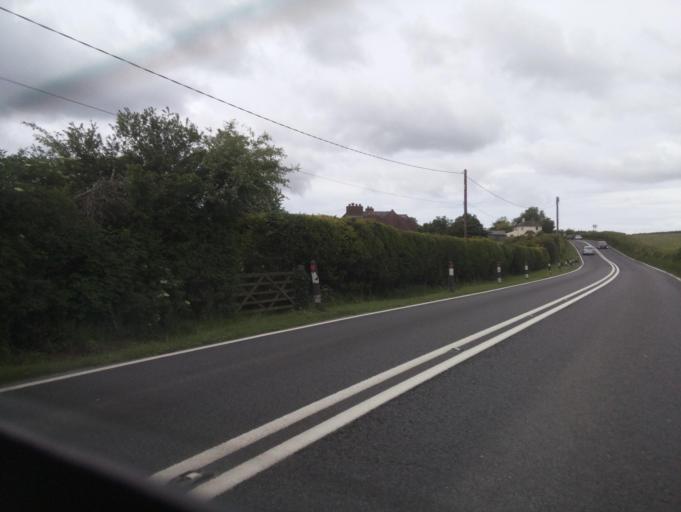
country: GB
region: England
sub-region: Dorset
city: Chickerell
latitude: 50.7152
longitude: -2.5276
